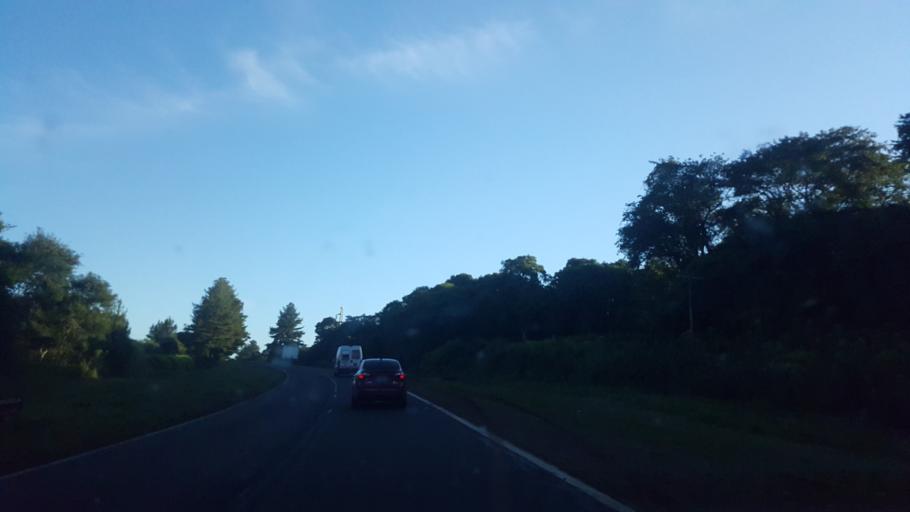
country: AR
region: Misiones
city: El Alcazar
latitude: -26.7473
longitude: -54.8832
